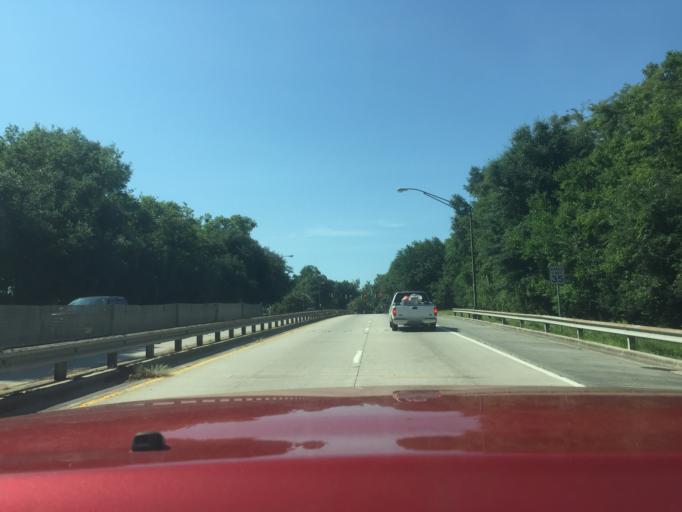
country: US
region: Georgia
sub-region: Chatham County
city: Savannah
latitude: 32.0625
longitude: -81.1112
